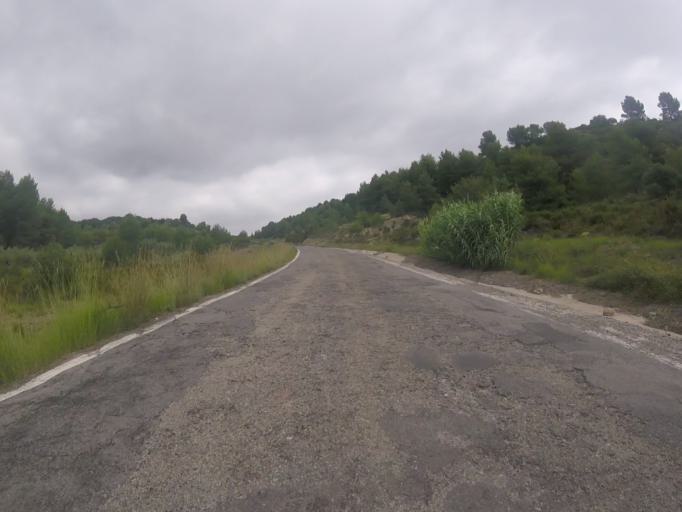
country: ES
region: Valencia
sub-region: Provincia de Castello
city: Cabanes
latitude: 40.1185
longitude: 0.0474
